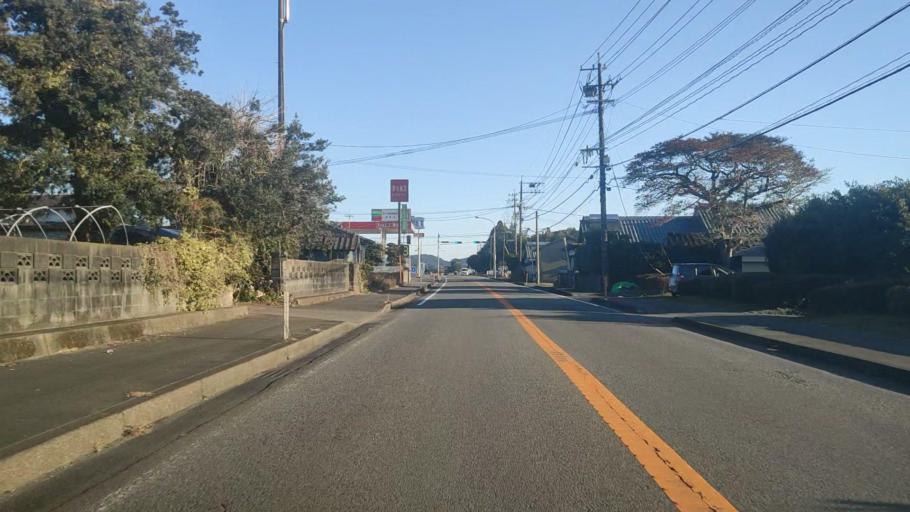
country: JP
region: Miyazaki
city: Takanabe
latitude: 32.3149
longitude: 131.5896
